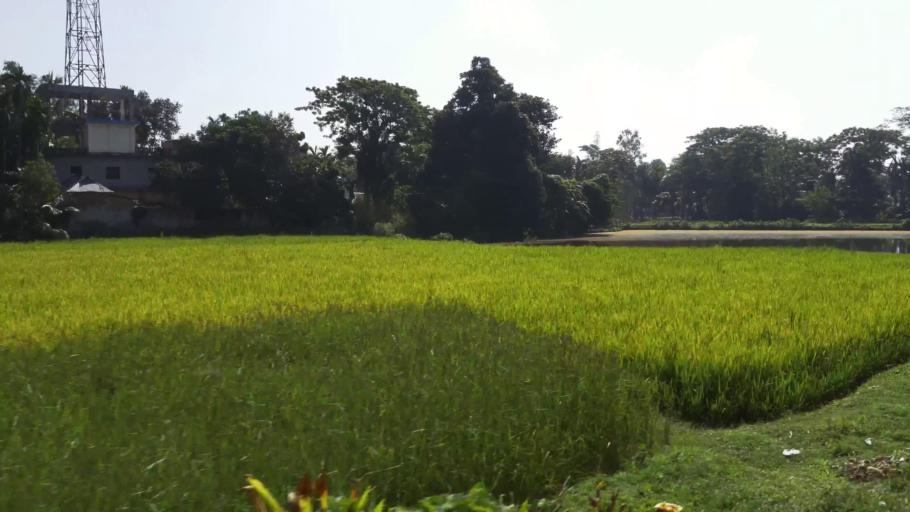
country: BD
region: Dhaka
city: Gafargaon
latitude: 24.4980
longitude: 90.5220
